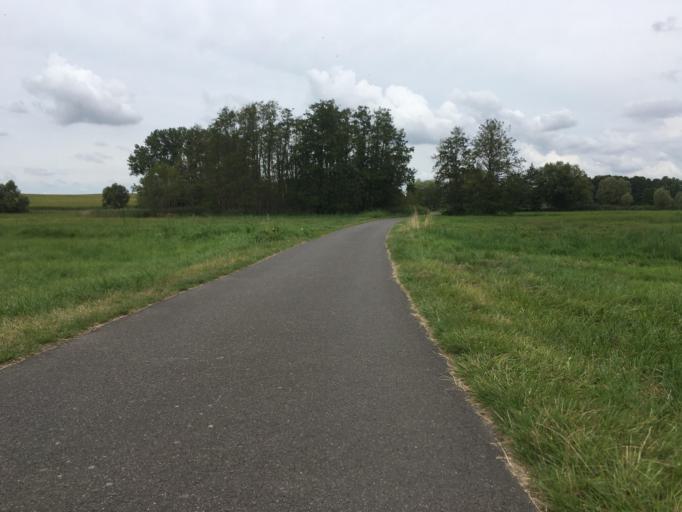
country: DE
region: Brandenburg
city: Prenzlau
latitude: 53.2727
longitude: 13.8467
